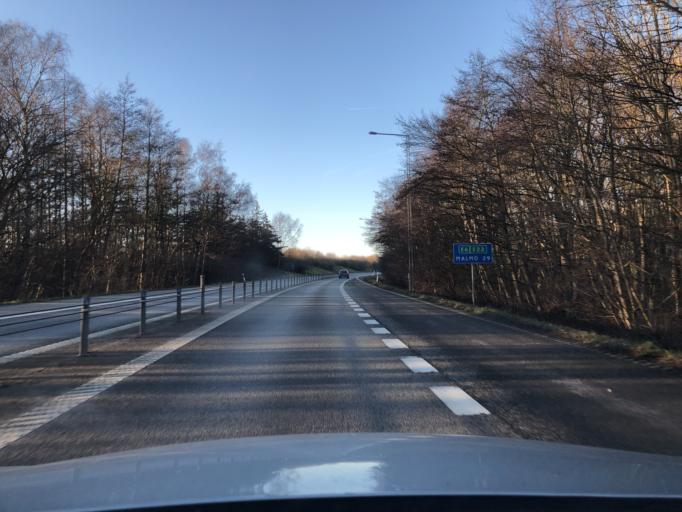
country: SE
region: Skane
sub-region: Trelleborgs Kommun
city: Skare
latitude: 55.3781
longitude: 13.0938
